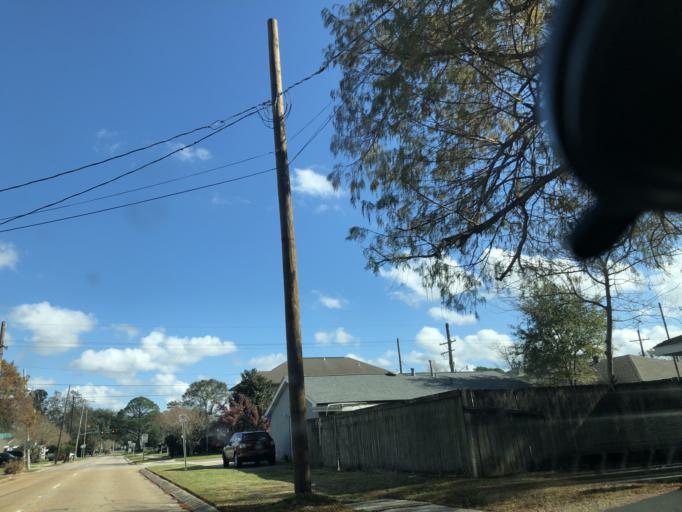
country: US
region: Louisiana
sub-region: Jefferson Parish
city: Metairie Terrace
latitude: 29.9815
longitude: -90.1621
